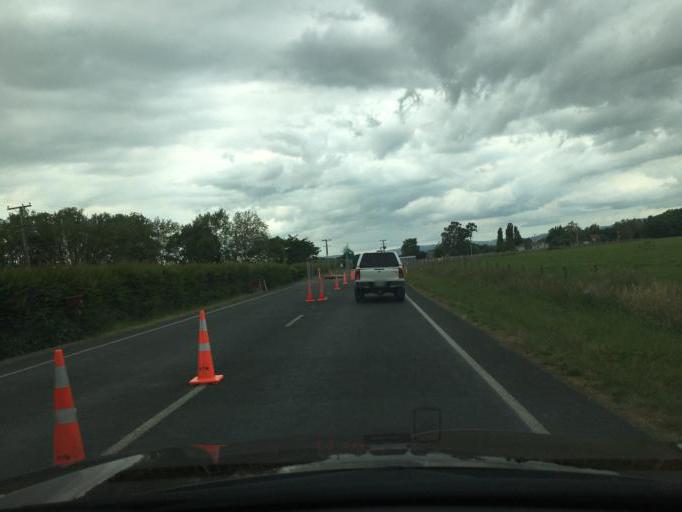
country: NZ
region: Waikato
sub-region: Waipa District
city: Cambridge
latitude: -37.9202
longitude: 175.4374
